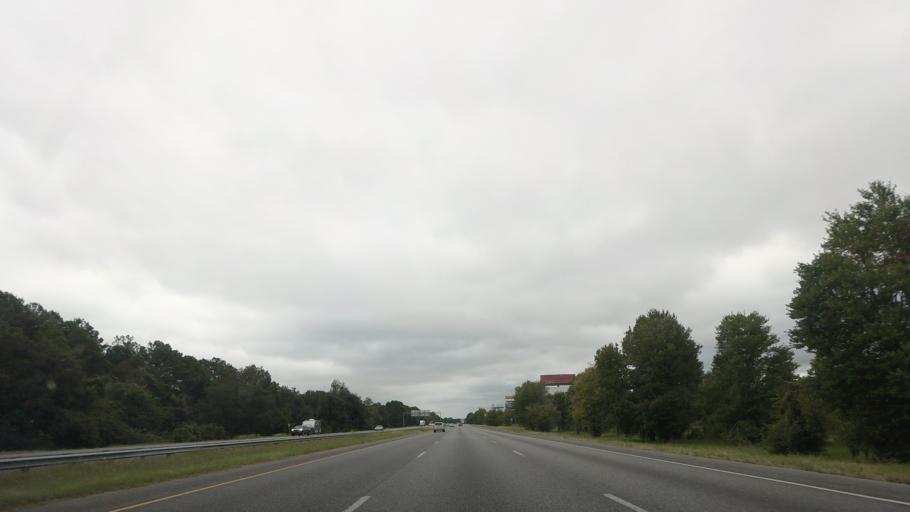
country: US
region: Georgia
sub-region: Echols County
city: Statenville
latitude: 30.6384
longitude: -83.1846
